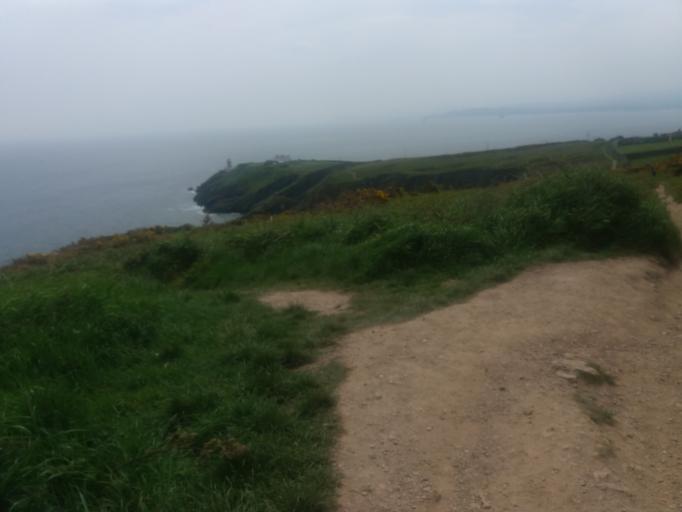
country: IE
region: Leinster
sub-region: Fingal County
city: Howth
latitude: 53.3691
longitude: -6.0538
